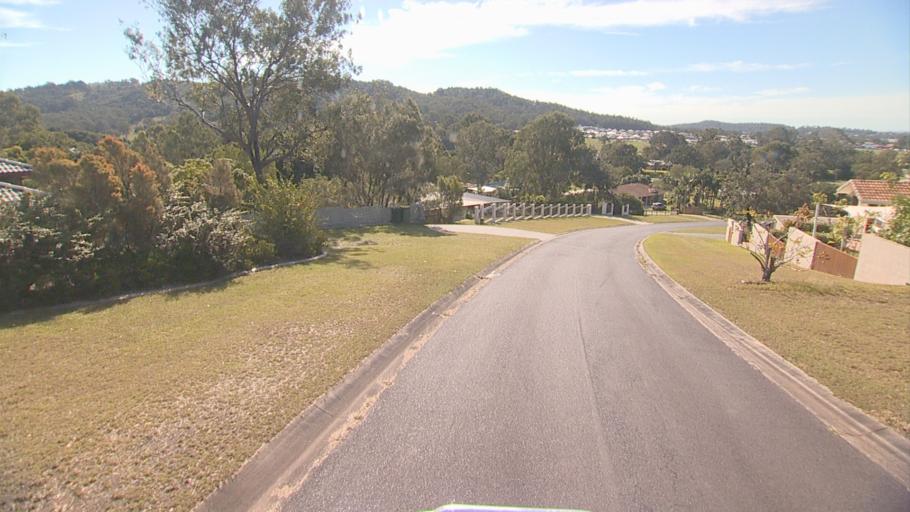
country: AU
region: Queensland
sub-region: Logan
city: Windaroo
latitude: -27.7603
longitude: 153.1797
